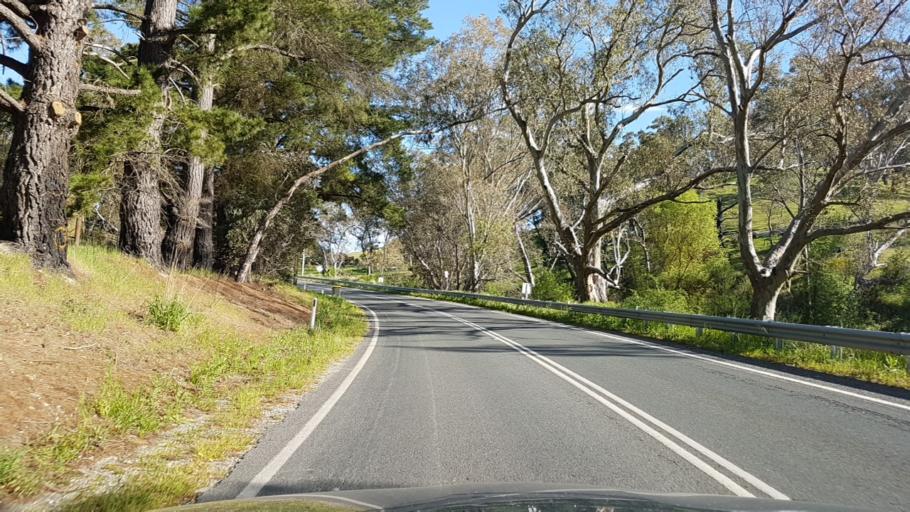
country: AU
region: South Australia
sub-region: Adelaide Hills
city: Gumeracha
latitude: -34.8320
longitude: 138.8909
